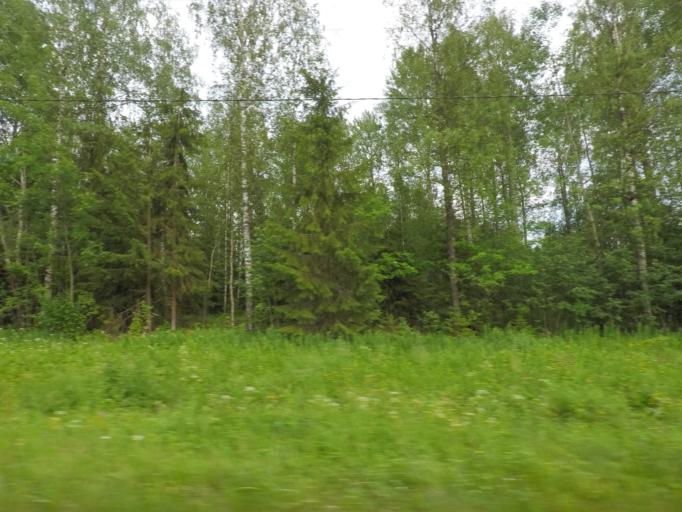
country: FI
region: Paijanne Tavastia
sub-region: Lahti
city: Hollola
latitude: 60.8904
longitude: 25.5160
